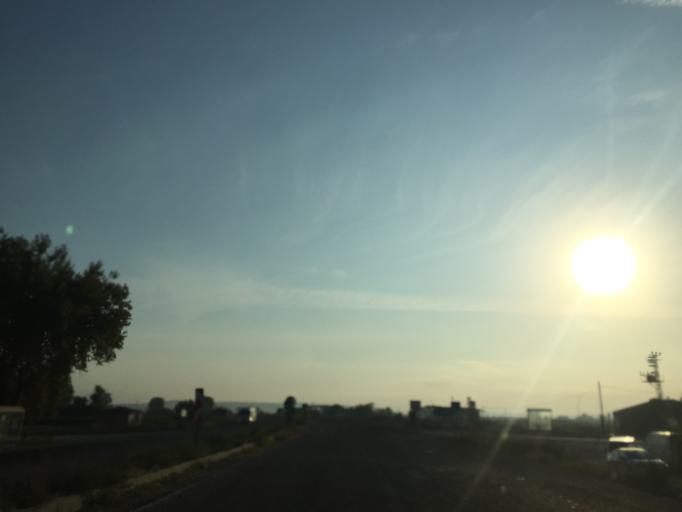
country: TR
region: Balikesir
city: Manyas
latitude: 40.0730
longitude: 28.0227
